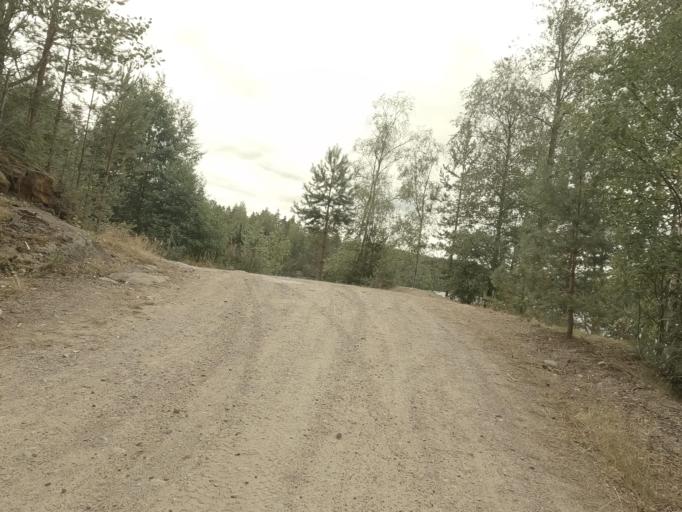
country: RU
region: Leningrad
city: Kamennogorsk
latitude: 61.0100
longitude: 29.1865
